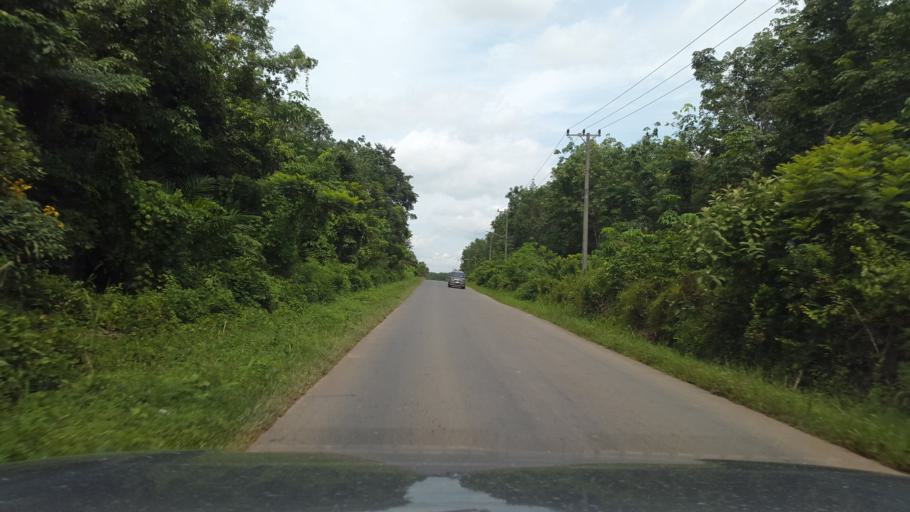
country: ID
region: South Sumatra
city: Gunungmegang Dalam
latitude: -3.3723
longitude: 103.9445
